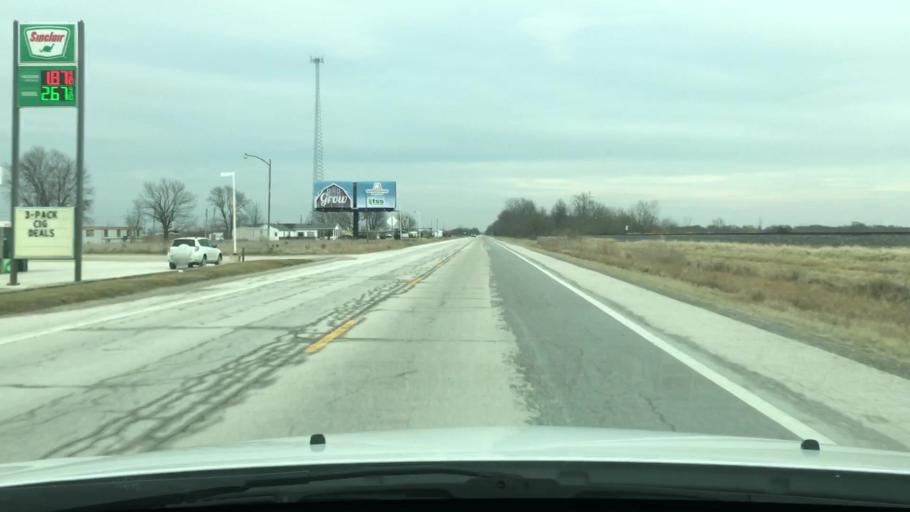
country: US
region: Missouri
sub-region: Audrain County
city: Vandalia
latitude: 39.3173
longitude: -91.4695
